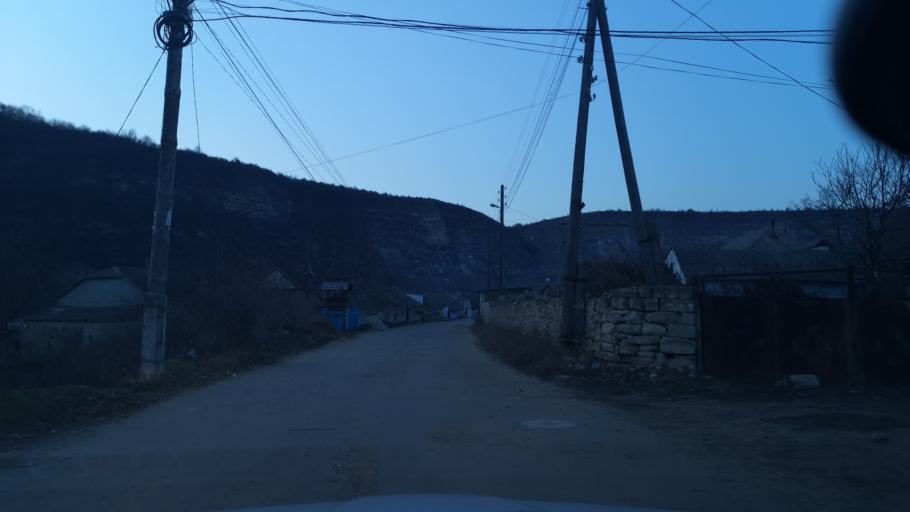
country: MD
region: Telenesti
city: Cocieri
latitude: 47.3030
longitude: 28.9641
